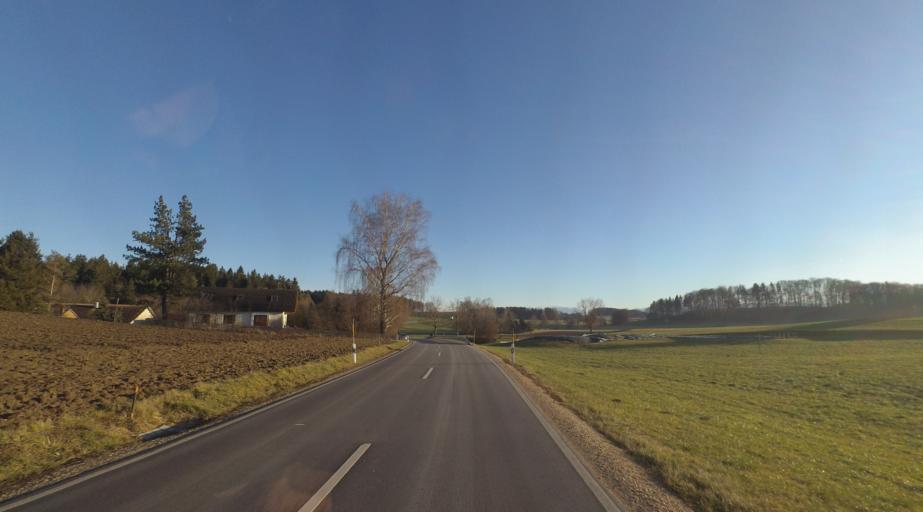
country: DE
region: Bavaria
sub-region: Upper Bavaria
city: Taching am See
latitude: 47.9928
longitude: 12.7624
